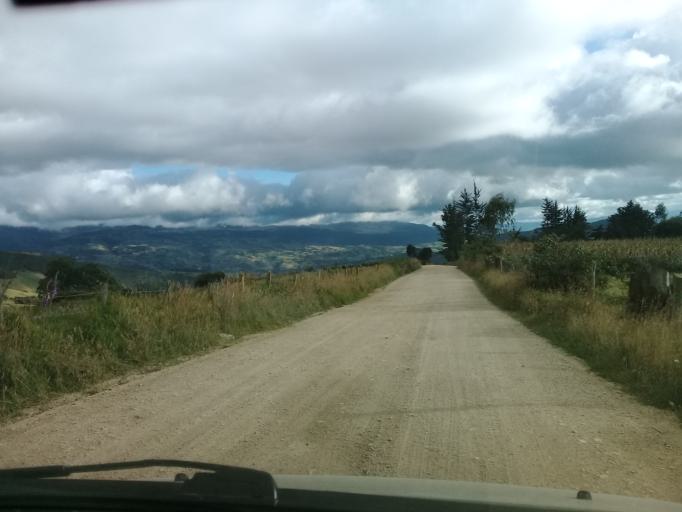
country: CO
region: Cundinamarca
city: Villapinzon
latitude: 5.2349
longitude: -73.6506
